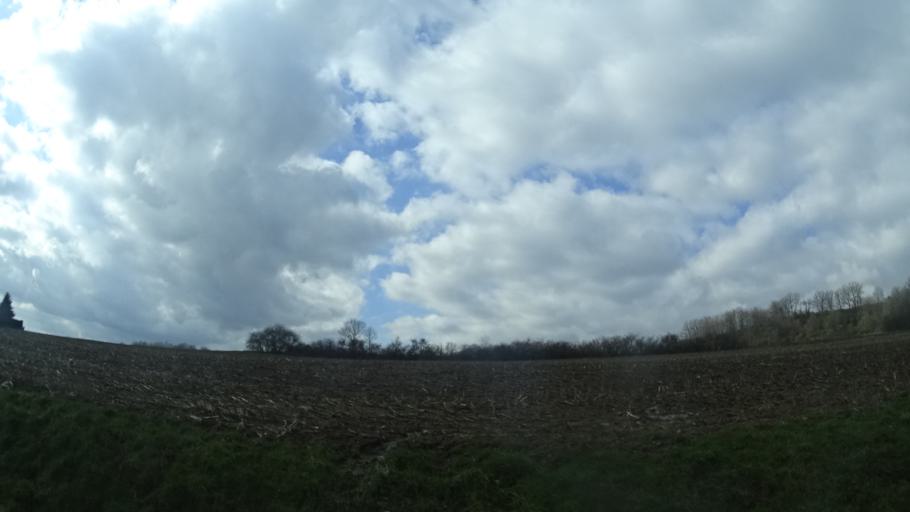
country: DE
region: Rheinland-Pfalz
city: Gollenberg
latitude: 49.6611
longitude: 7.1634
